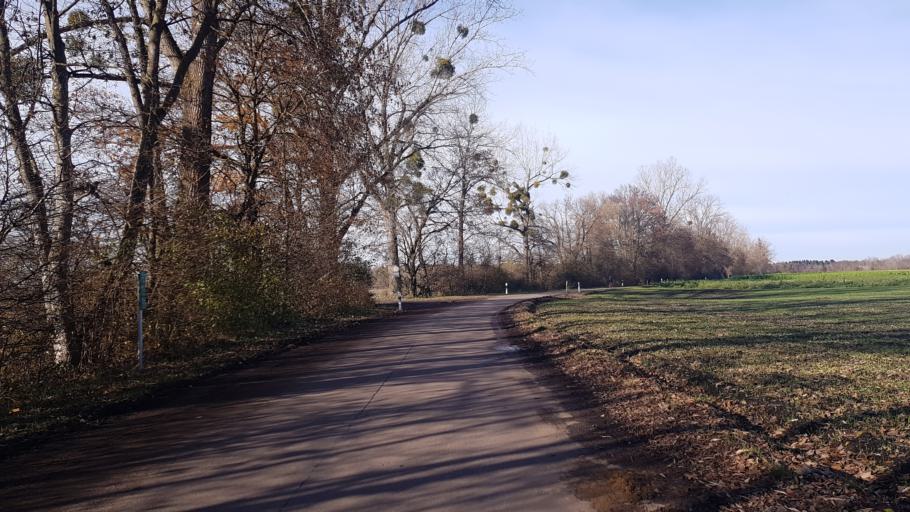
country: DE
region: Bavaria
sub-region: Upper Bavaria
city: Karlsfeld
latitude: 48.2302
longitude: 11.5068
